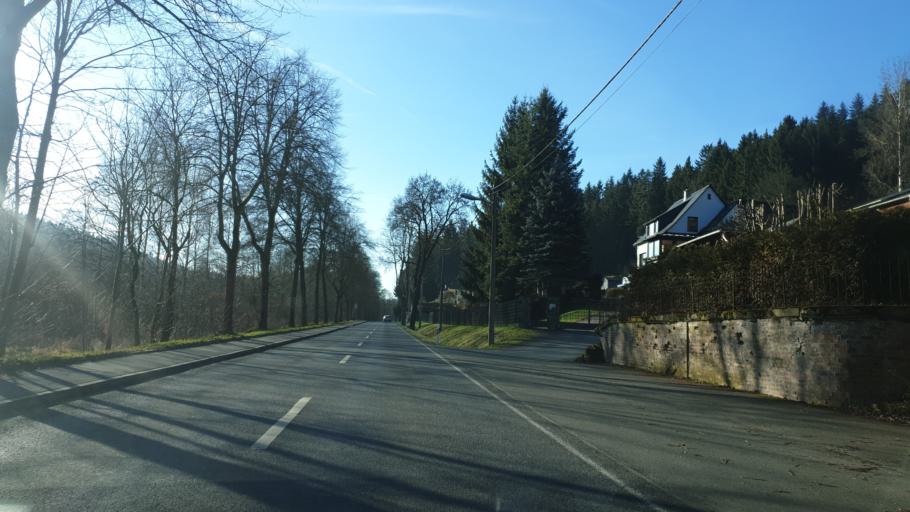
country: DE
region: Saxony
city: Bad Elster
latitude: 50.2975
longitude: 12.2486
